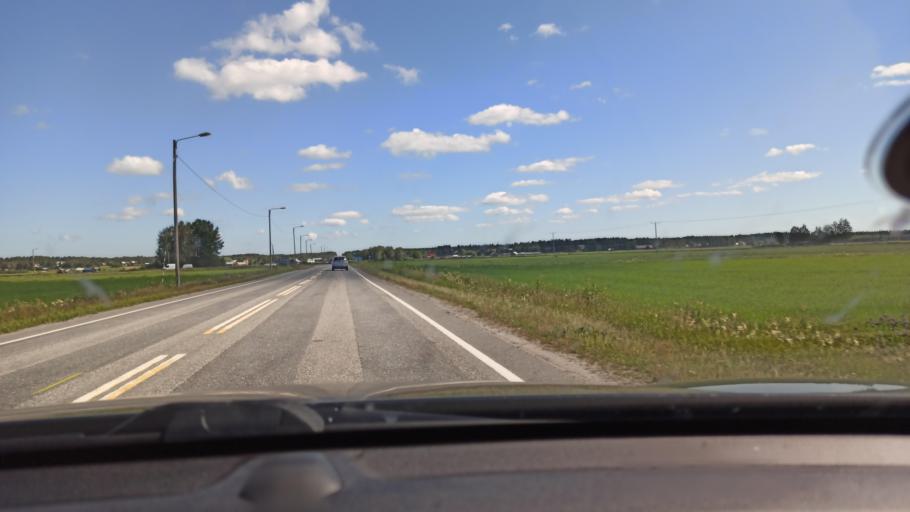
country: FI
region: Ostrobothnia
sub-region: Vaasa
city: Teeriniemi
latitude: 63.0024
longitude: 21.6756
